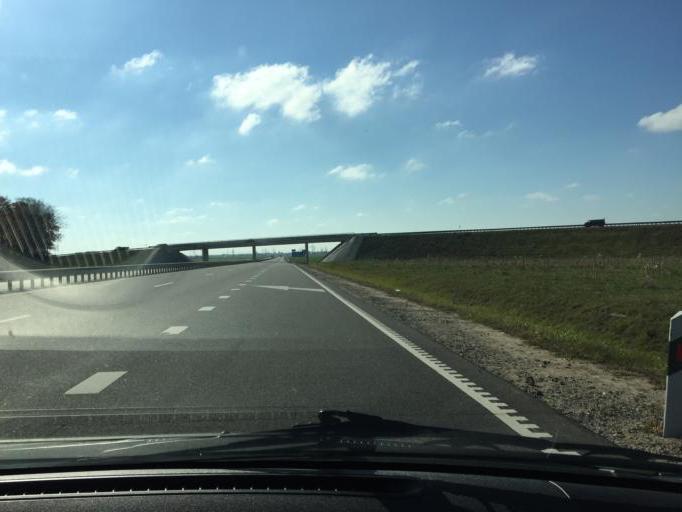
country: BY
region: Minsk
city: Slutsk
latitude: 53.0693
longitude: 27.5541
